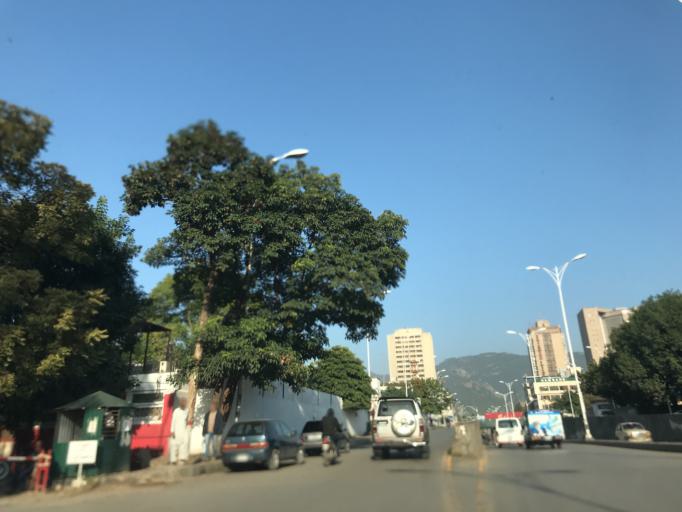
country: PK
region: Islamabad
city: Islamabad
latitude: 33.7208
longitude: 73.0839
